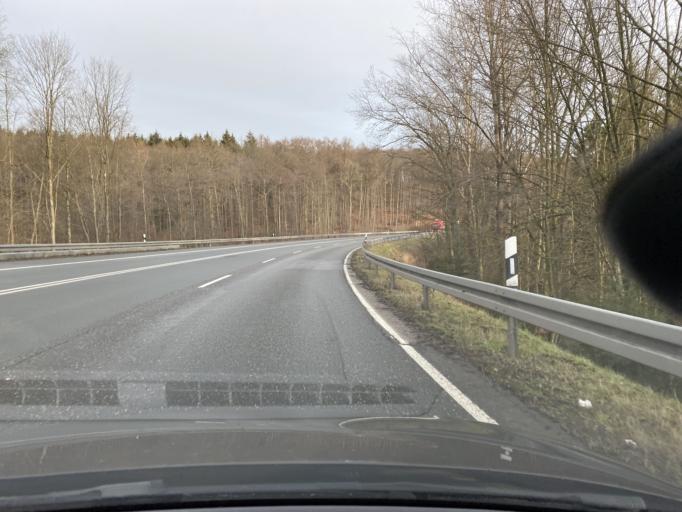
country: DE
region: North Rhine-Westphalia
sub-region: Regierungsbezirk Arnsberg
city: Meschede
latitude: 51.3745
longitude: 8.2921
